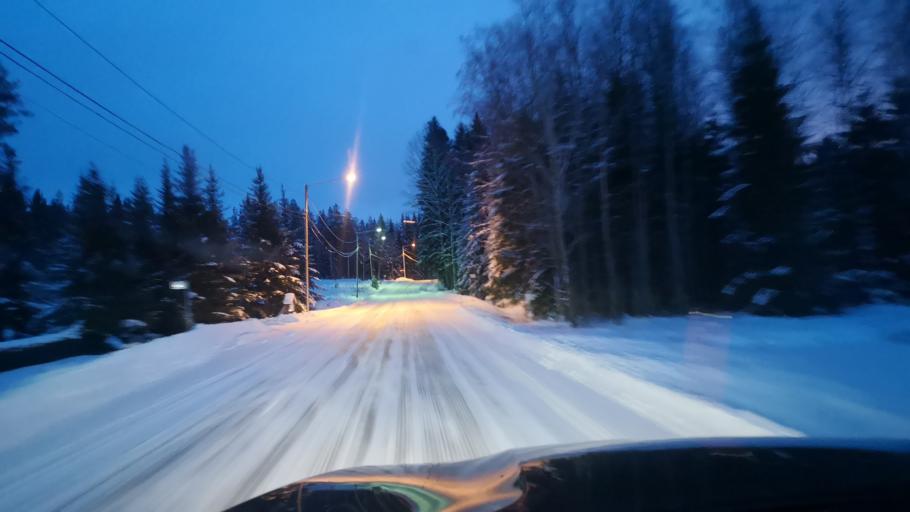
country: FI
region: Varsinais-Suomi
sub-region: Loimaa
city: Loimaa
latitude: 60.8722
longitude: 23.0900
